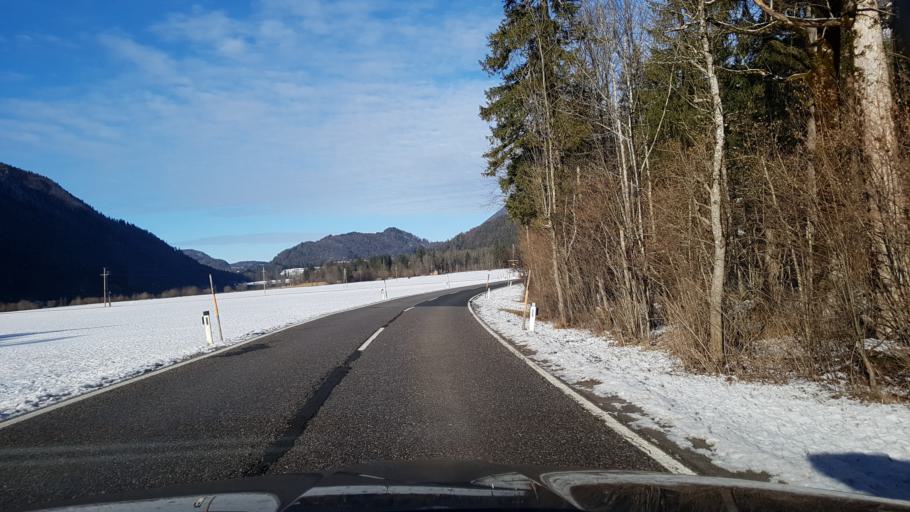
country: AT
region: Salzburg
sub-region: Politischer Bezirk Salzburg-Umgebung
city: Faistenau
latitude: 47.7401
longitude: 13.2580
